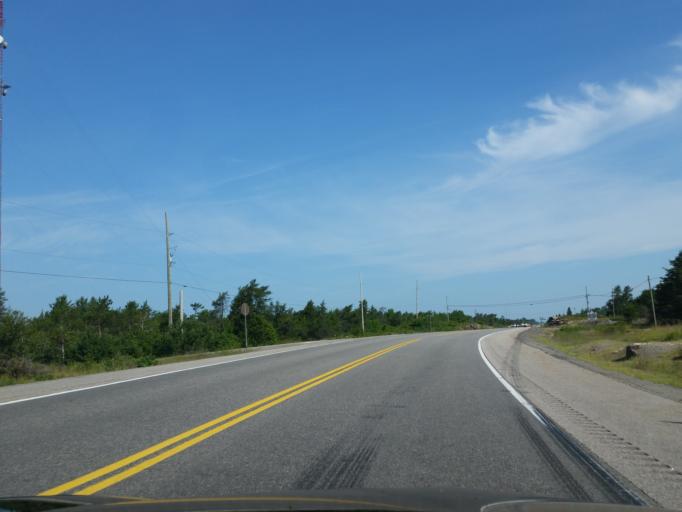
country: CA
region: Ontario
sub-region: Parry Sound District
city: Parry Sound
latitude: 45.7939
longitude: -80.5323
